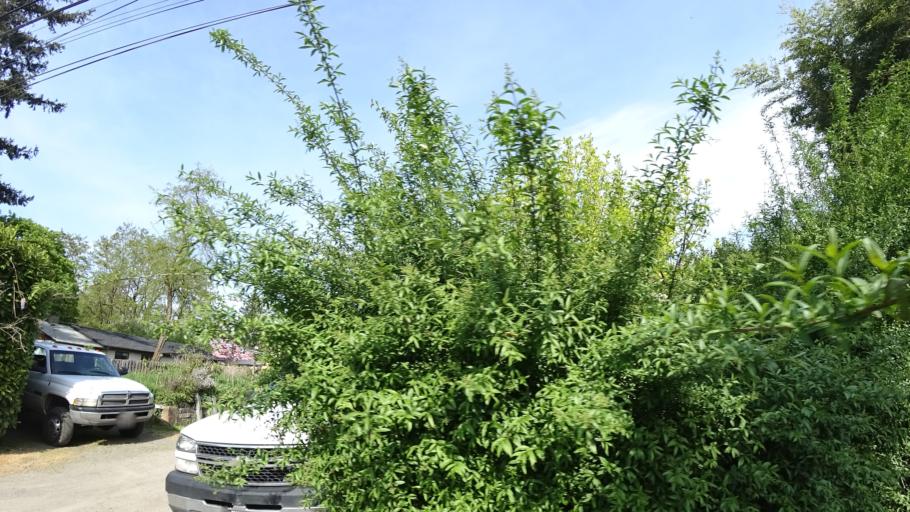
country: US
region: Oregon
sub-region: Clackamas County
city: Milwaukie
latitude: 45.4748
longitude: -122.6146
